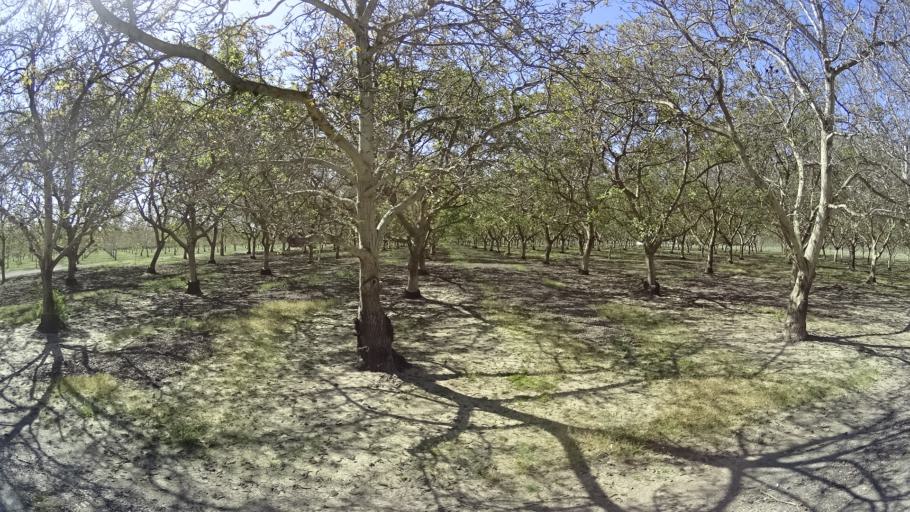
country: US
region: California
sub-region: Glenn County
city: Hamilton City
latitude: 39.7216
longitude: -122.0157
